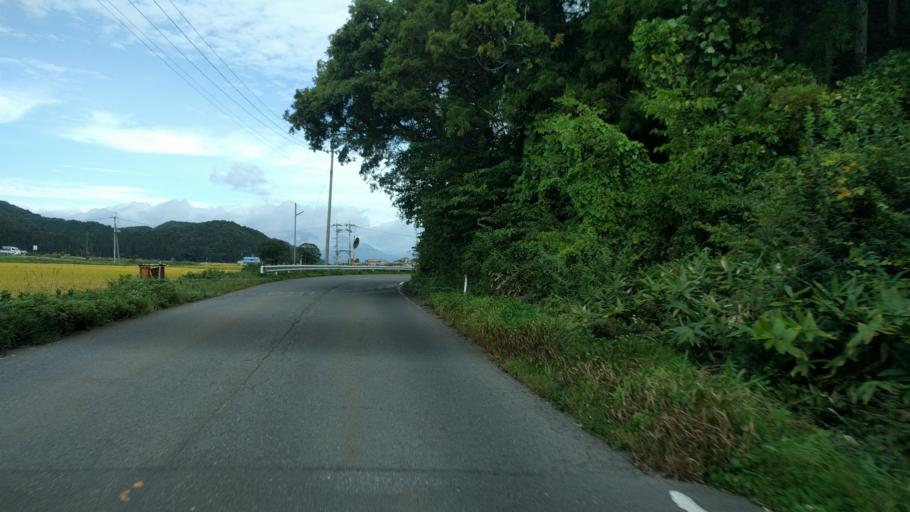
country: JP
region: Fukushima
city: Inawashiro
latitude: 37.3886
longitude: 140.1287
